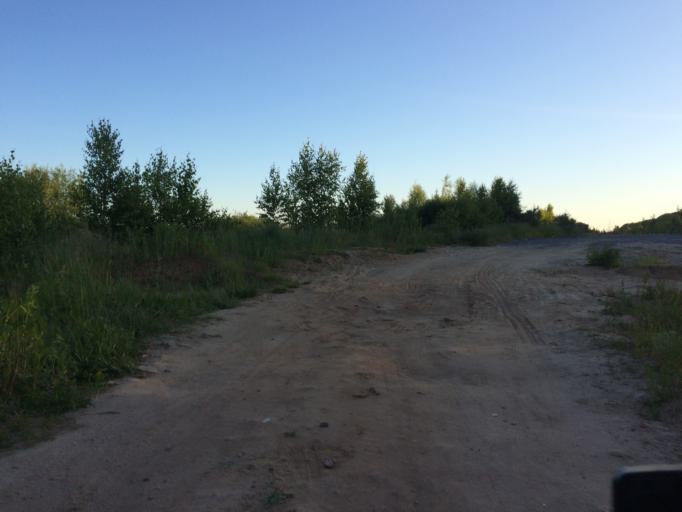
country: RU
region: Mariy-El
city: Yoshkar-Ola
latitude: 56.6552
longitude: 47.8982
